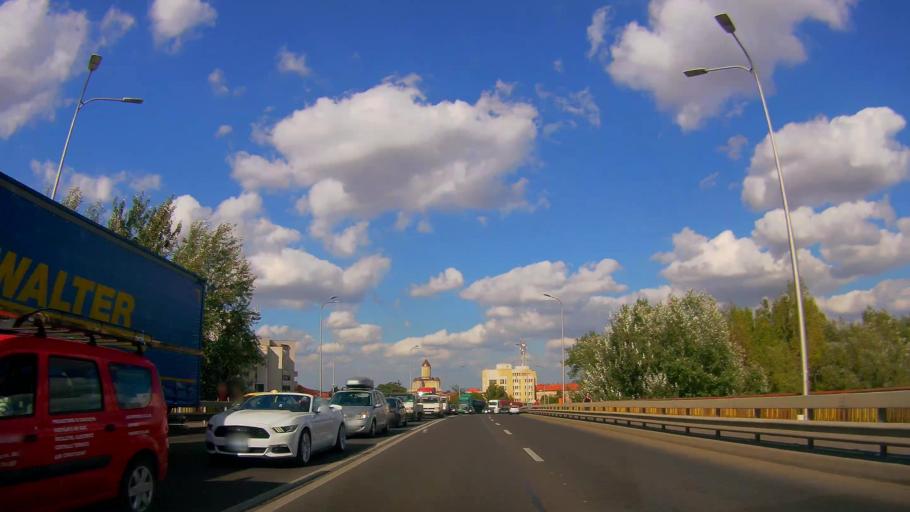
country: RO
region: Satu Mare
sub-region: Municipiul Satu Mare
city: Satu Mare
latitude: 47.7870
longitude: 22.8783
